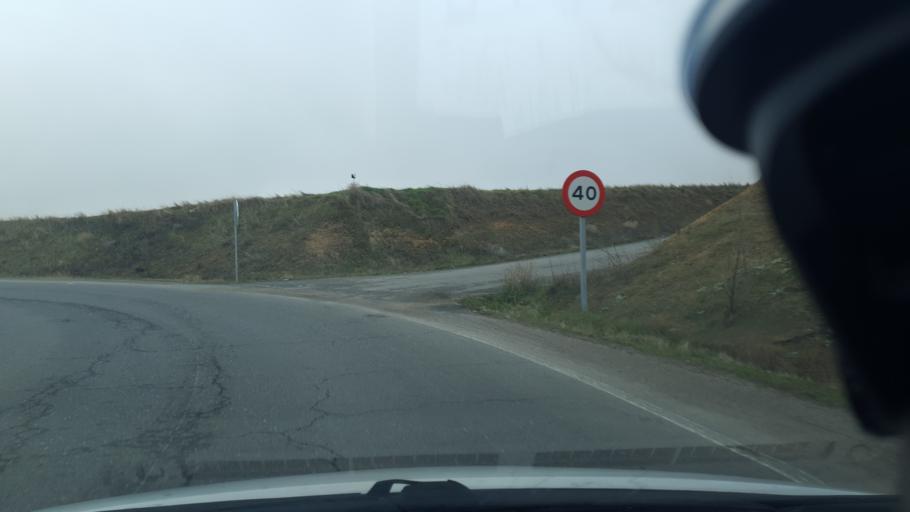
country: ES
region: Castille and Leon
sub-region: Provincia de Segovia
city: Encinillas
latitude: 41.0019
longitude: -4.1560
